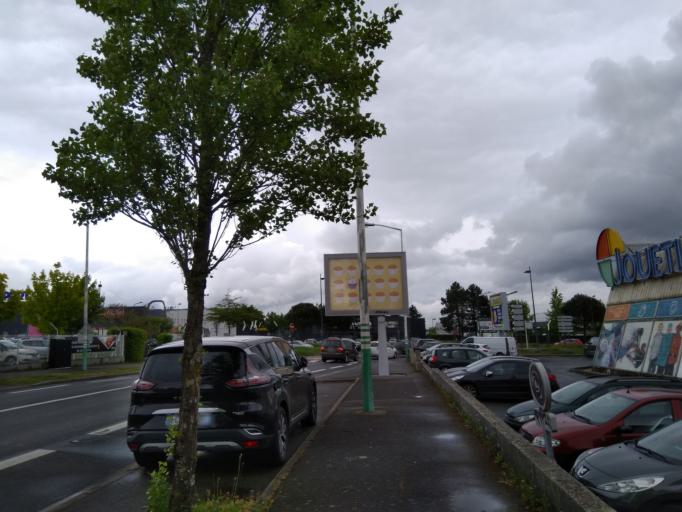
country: FR
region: Pays de la Loire
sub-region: Departement de la Loire-Atlantique
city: Orvault
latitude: 47.2490
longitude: -1.6148
